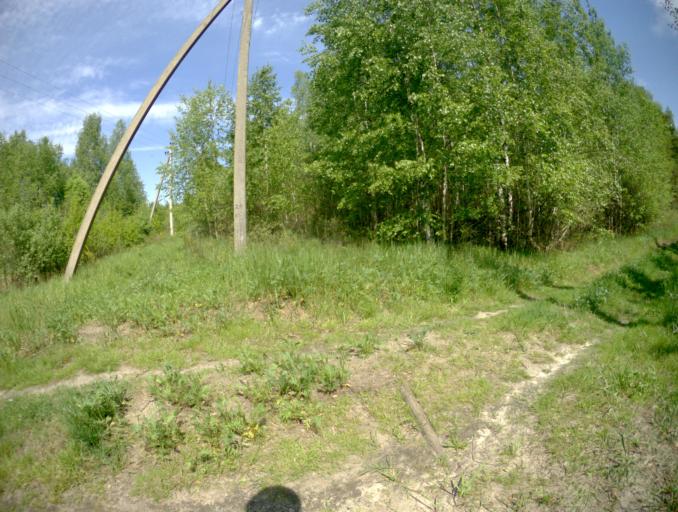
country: RU
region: Vladimir
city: Gusevskiy
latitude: 55.6717
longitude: 40.4611
